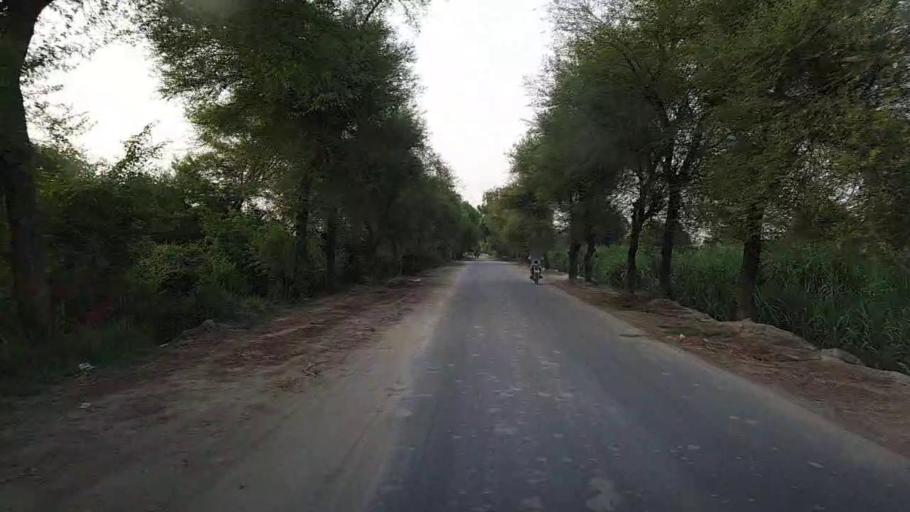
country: PK
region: Sindh
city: Ubauro
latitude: 28.2877
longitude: 69.8001
